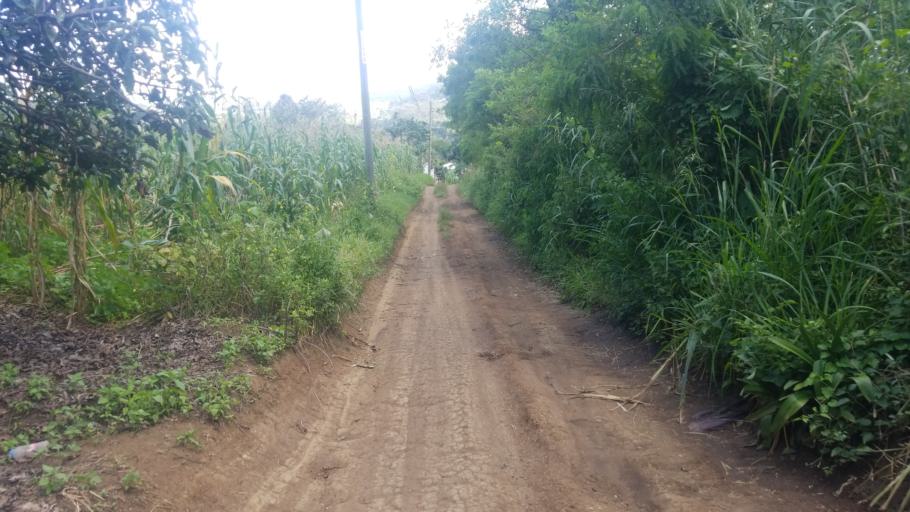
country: GT
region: Guatemala
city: Amatitlan
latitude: 14.5019
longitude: -90.6439
